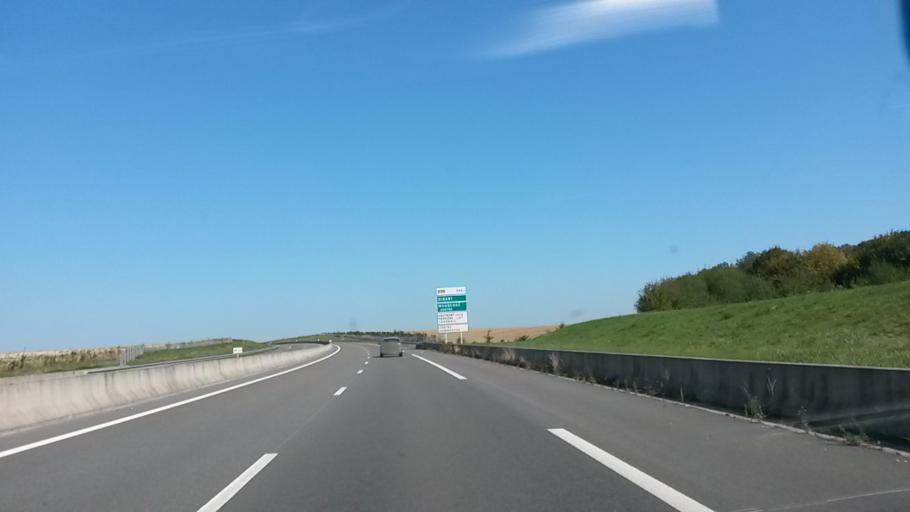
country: FR
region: Nord-Pas-de-Calais
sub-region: Departement du Nord
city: Louvroil
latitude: 50.2339
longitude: 3.9623
